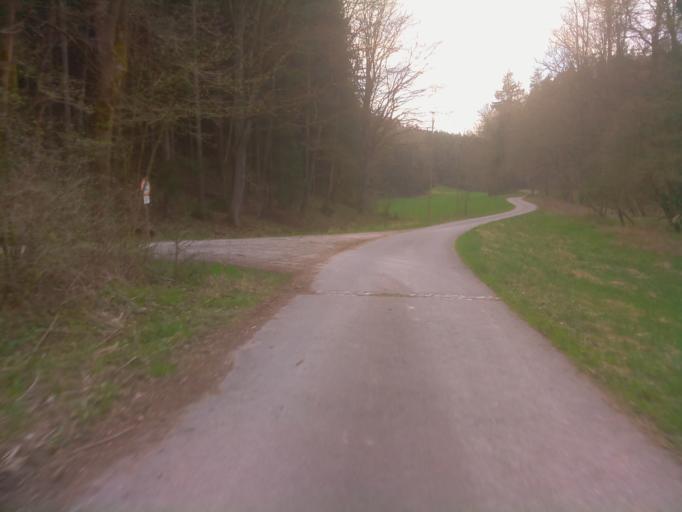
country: DE
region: Thuringia
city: Unterbodnitz
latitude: 50.8307
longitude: 11.6441
